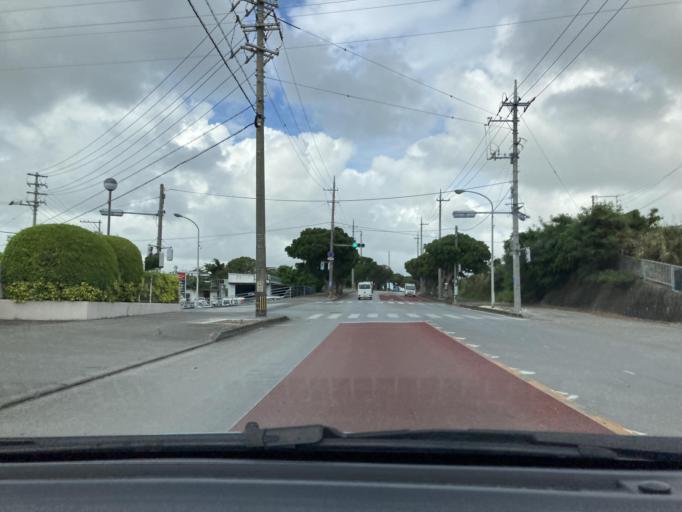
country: JP
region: Okinawa
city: Itoman
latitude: 26.1372
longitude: 127.6880
